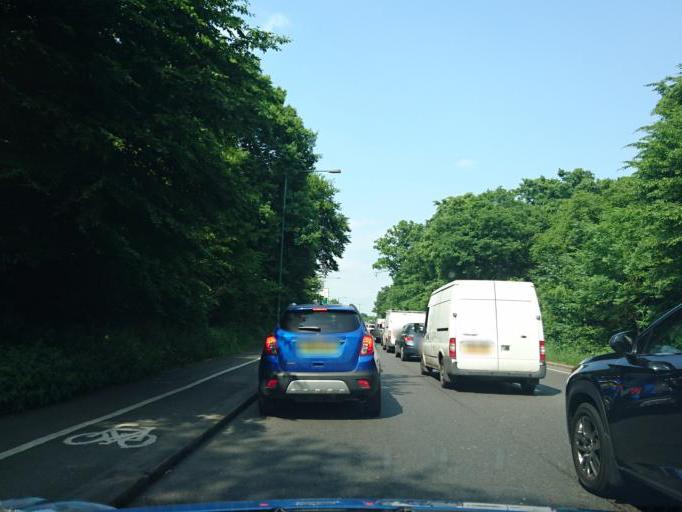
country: GB
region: England
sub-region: Greater London
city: Woodford Green
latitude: 51.5920
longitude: 0.0091
